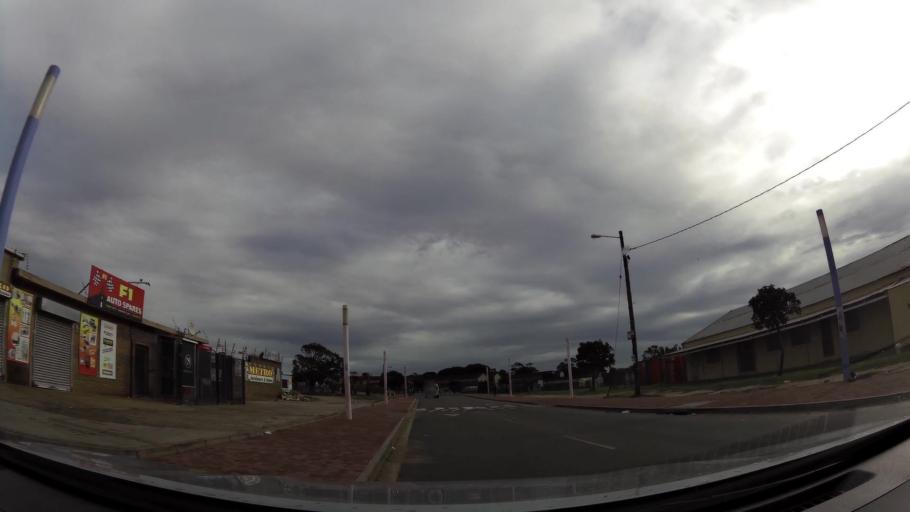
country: ZA
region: Eastern Cape
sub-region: Nelson Mandela Bay Metropolitan Municipality
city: Port Elizabeth
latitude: -33.9862
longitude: 25.5881
